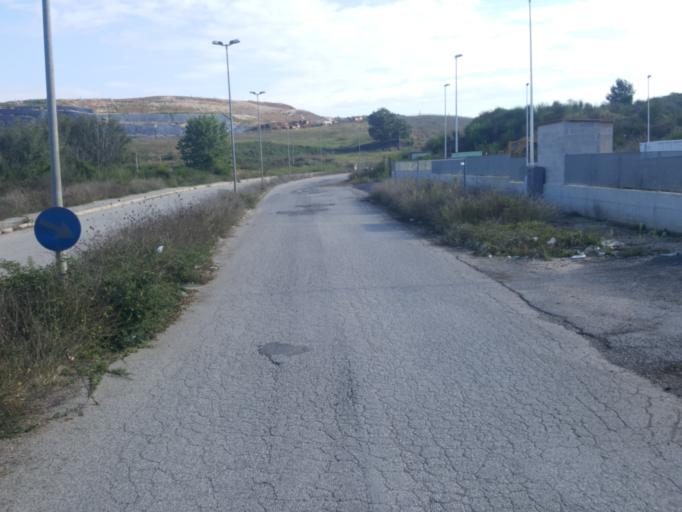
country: IT
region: Latium
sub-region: Citta metropolitana di Roma Capitale
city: Colleferro
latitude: 41.7569
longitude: 12.9978
